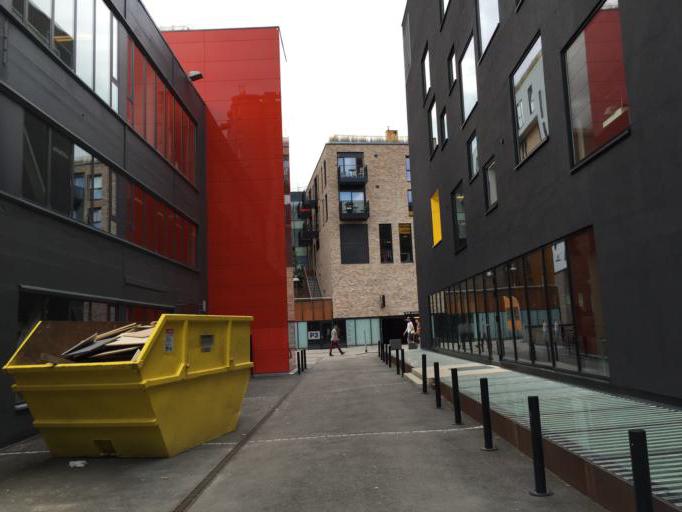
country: NO
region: Oslo
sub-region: Oslo
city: Oslo
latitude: 59.9232
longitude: 10.7528
